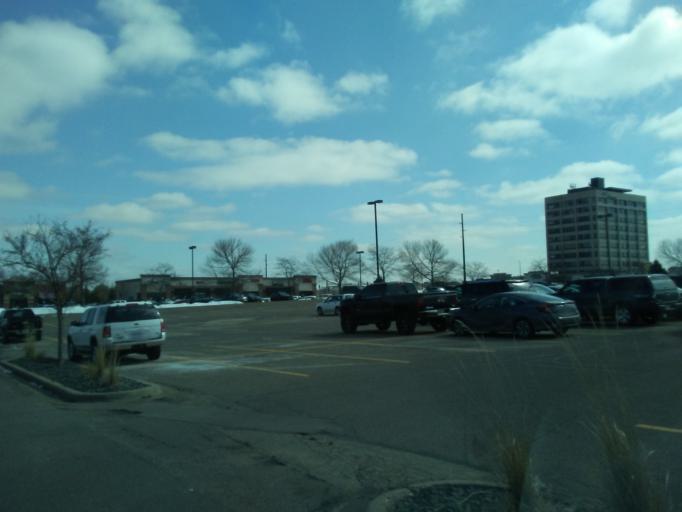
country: US
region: Minnesota
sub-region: Dakota County
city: Eagan
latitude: 44.8349
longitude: -93.1559
